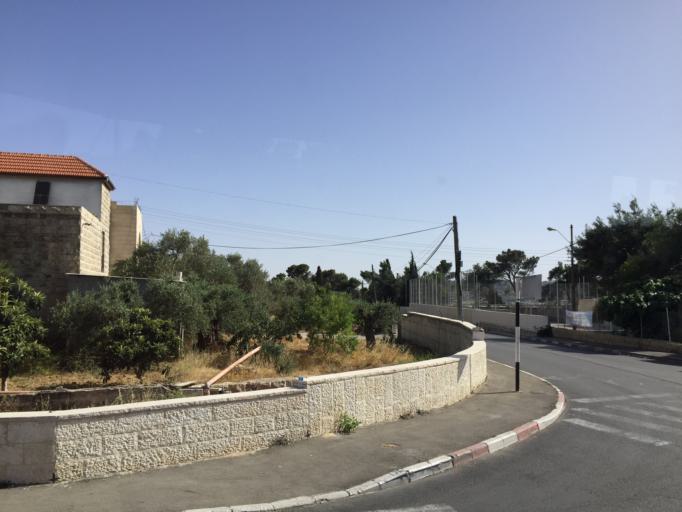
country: PS
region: West Bank
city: Bayt Jala
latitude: 31.7163
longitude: 35.1766
